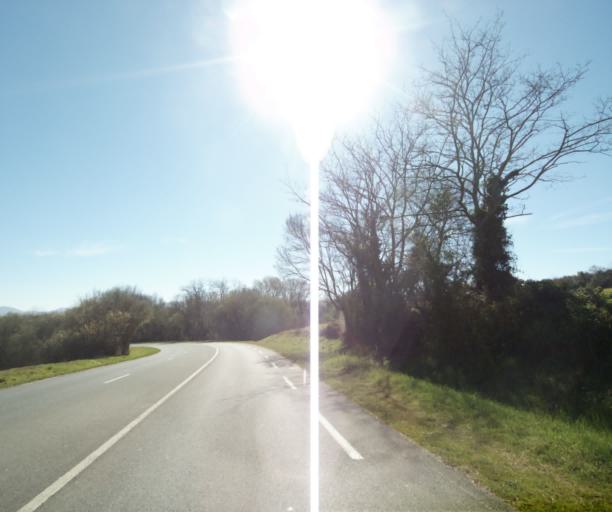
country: FR
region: Aquitaine
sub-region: Departement des Pyrenees-Atlantiques
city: Urrugne
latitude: 43.3881
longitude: -1.7000
